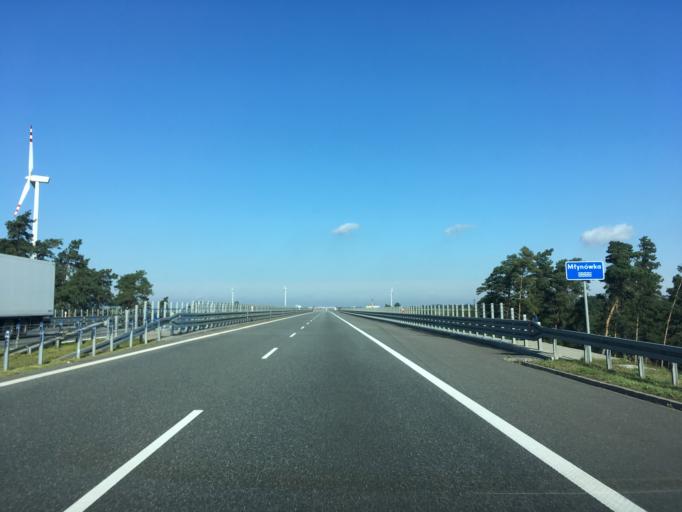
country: PL
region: Kujawsko-Pomorskie
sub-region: Powiat chelminski
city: Lisewo
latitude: 53.3594
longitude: 18.7010
